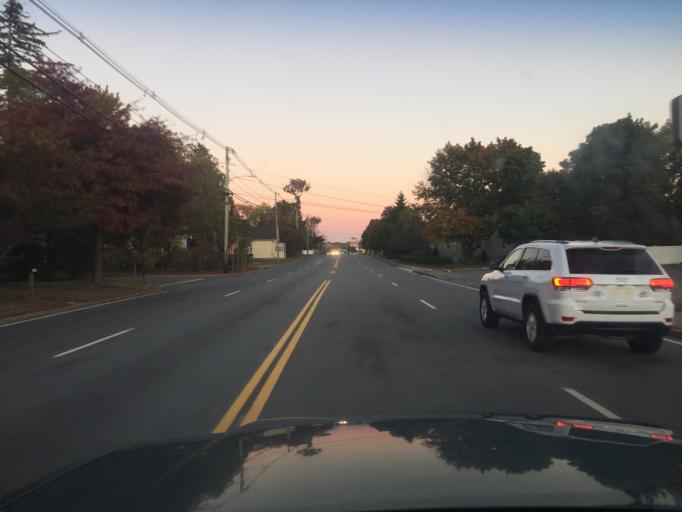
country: US
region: Massachusetts
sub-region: Worcester County
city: Milford
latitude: 42.1488
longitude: -71.4962
